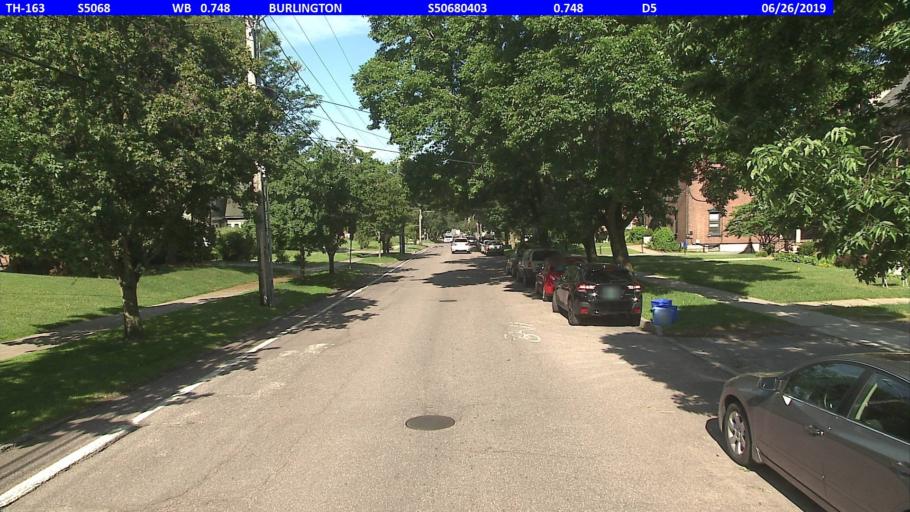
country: US
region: Vermont
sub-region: Chittenden County
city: Burlington
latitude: 44.4776
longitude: -73.2040
